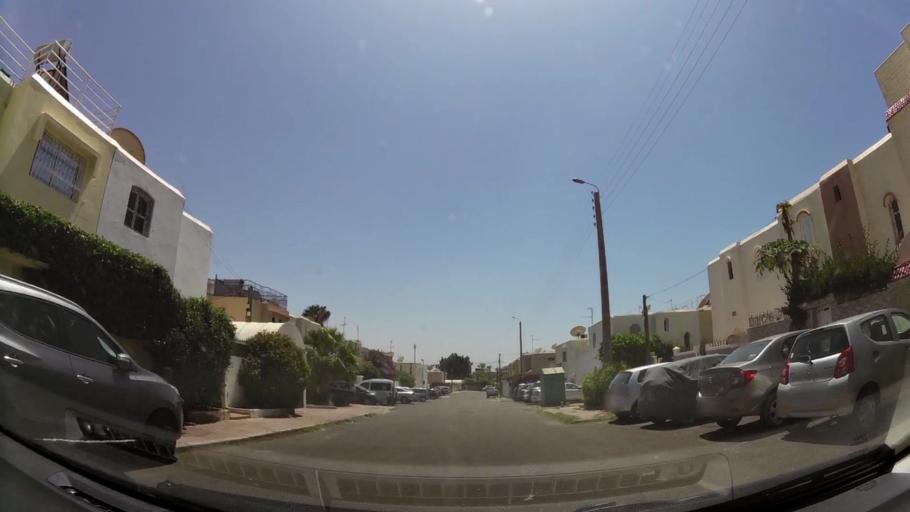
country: MA
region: Souss-Massa-Draa
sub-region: Agadir-Ida-ou-Tnan
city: Agadir
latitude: 30.4326
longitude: -9.5886
